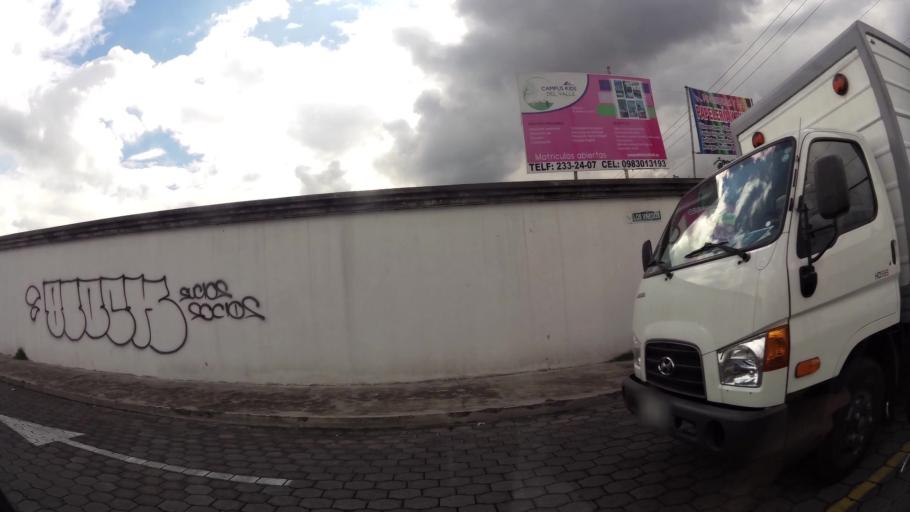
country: EC
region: Pichincha
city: Sangolqui
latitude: -0.3249
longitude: -78.4566
